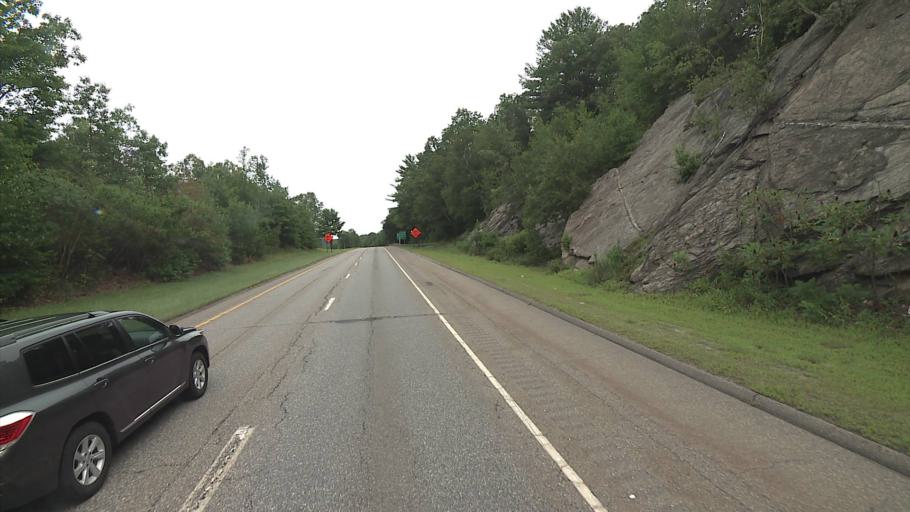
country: US
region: Connecticut
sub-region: Litchfield County
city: Thomaston
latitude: 41.7179
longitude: -73.0938
